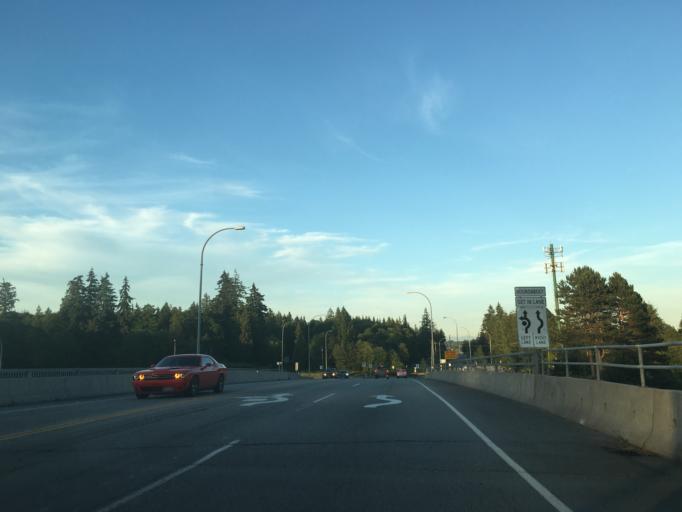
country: US
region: Washington
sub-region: Whatcom County
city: Blaine
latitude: 49.0166
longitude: -122.7603
